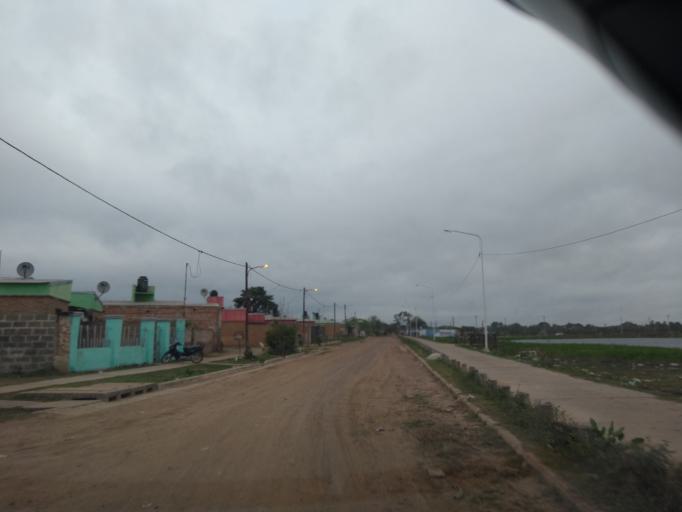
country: AR
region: Chaco
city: Resistencia
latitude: -27.4601
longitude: -58.9636
